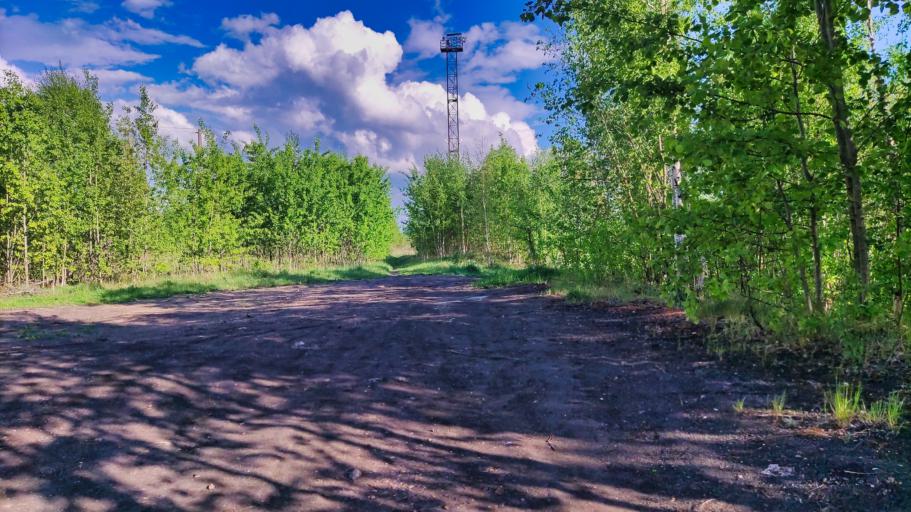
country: RU
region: Tverskaya
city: Rzhev
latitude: 56.2400
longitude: 34.3416
